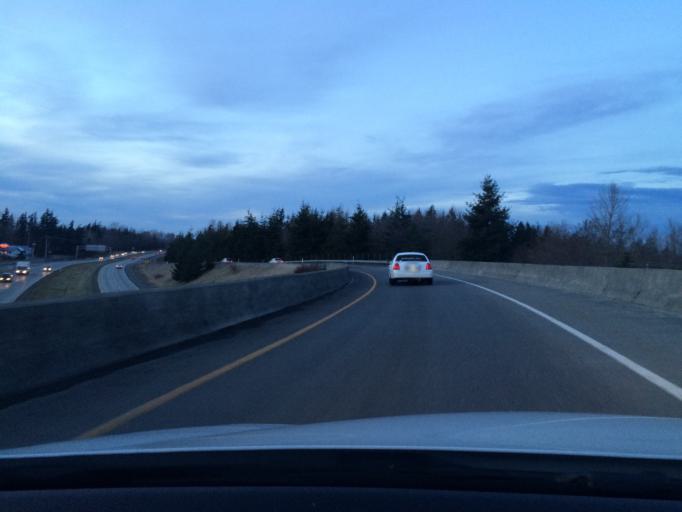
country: US
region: Washington
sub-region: Whatcom County
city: Marietta-Alderwood
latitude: 48.7894
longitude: -122.5190
